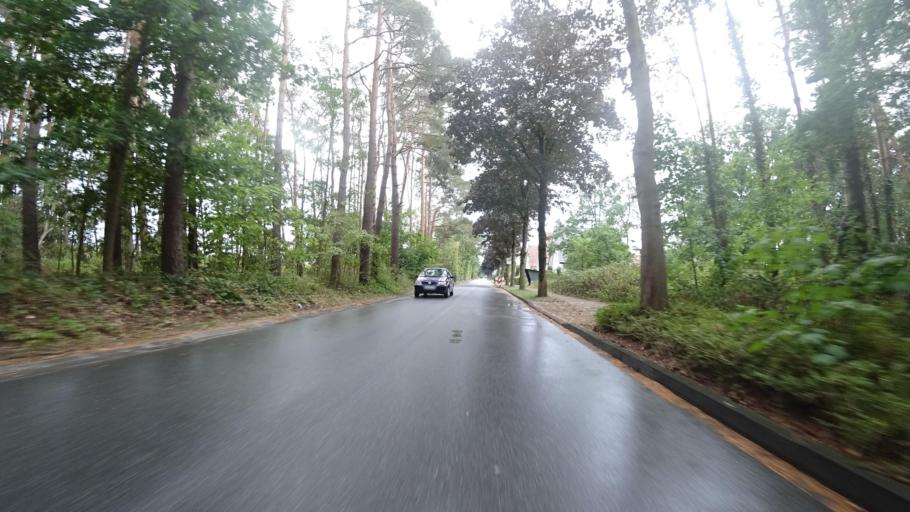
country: DE
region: North Rhine-Westphalia
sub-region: Regierungsbezirk Detmold
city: Rheda-Wiedenbruck
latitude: 51.8956
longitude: 8.2994
